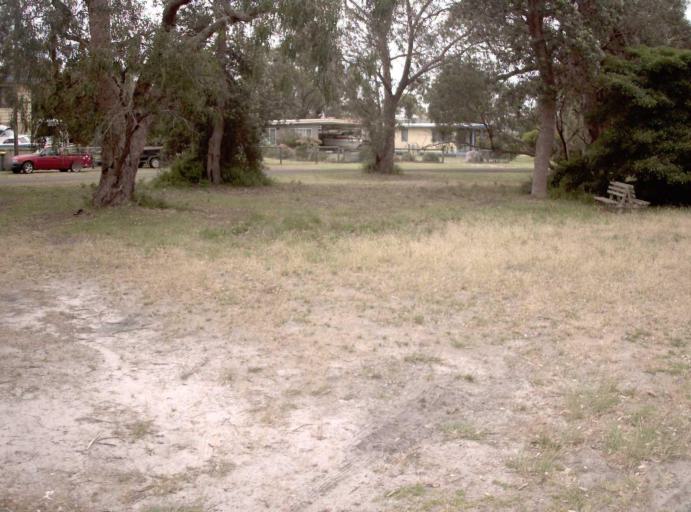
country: AU
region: Victoria
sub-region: East Gippsland
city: Bairnsdale
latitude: -38.0566
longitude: 147.5700
